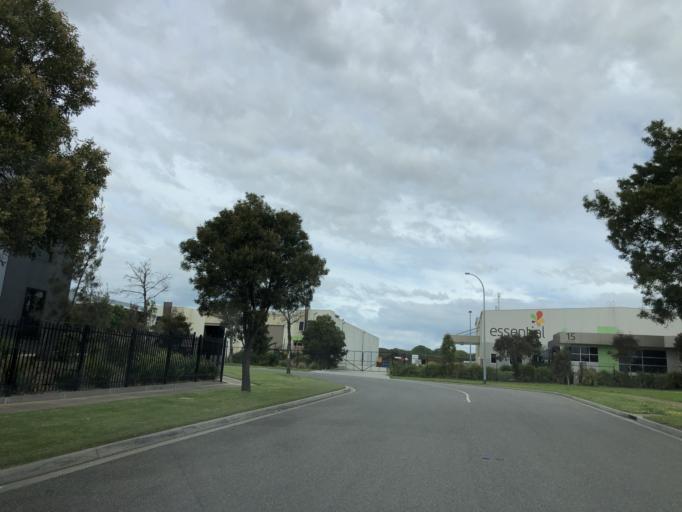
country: AU
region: Victoria
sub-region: Frankston
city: Carrum Downs
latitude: -38.0927
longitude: 145.1680
